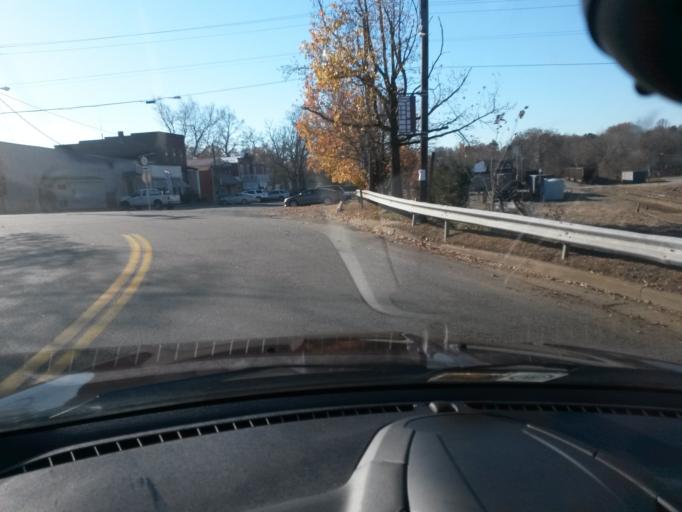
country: US
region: Virginia
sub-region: Charlotte County
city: Charlotte Court House
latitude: 37.0408
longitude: -78.4843
